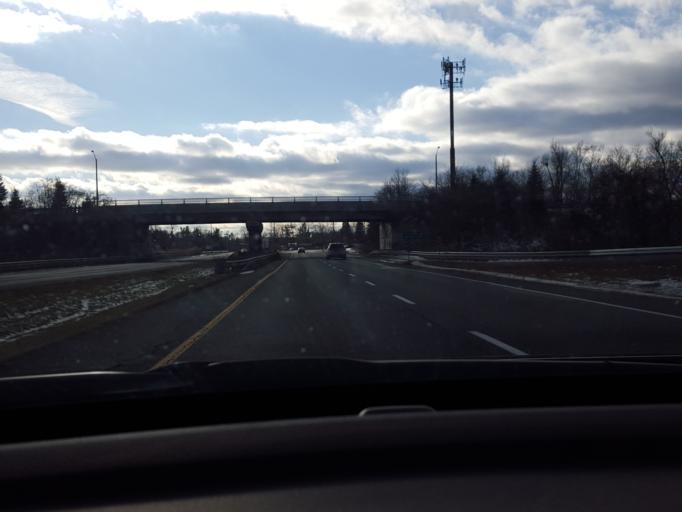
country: CA
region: Ontario
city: Scarborough
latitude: 43.7842
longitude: -79.1659
